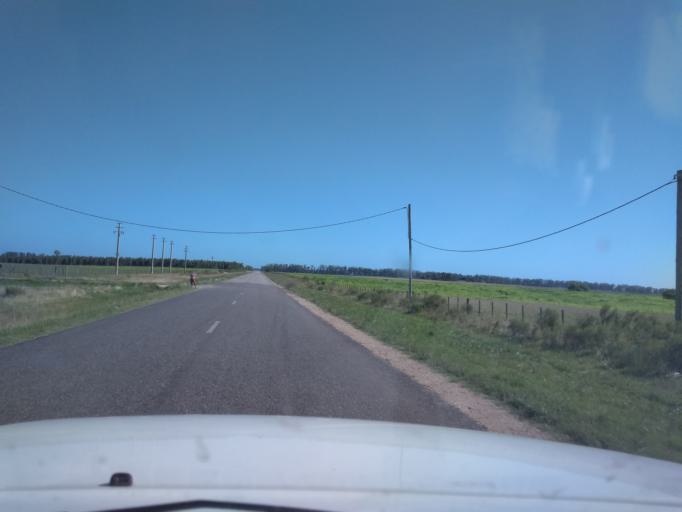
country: UY
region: Canelones
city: San Ramon
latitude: -34.1543
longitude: -55.9464
